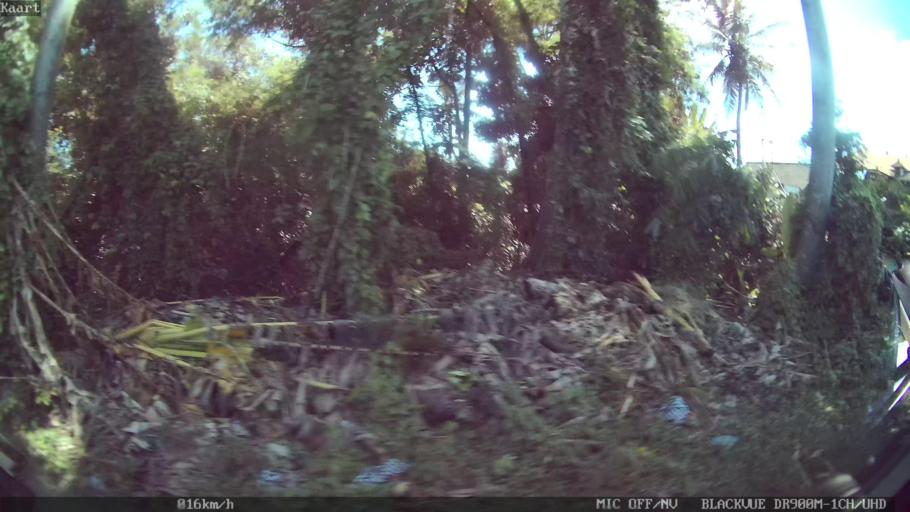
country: ID
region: Bali
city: Banjar Kelodan
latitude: -8.5531
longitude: 115.3354
